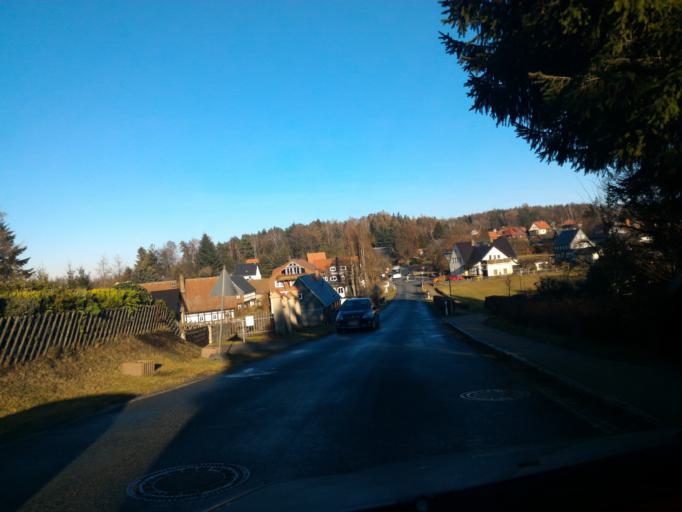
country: DE
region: Saxony
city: Kurort Jonsdorf
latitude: 50.8531
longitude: 14.6942
